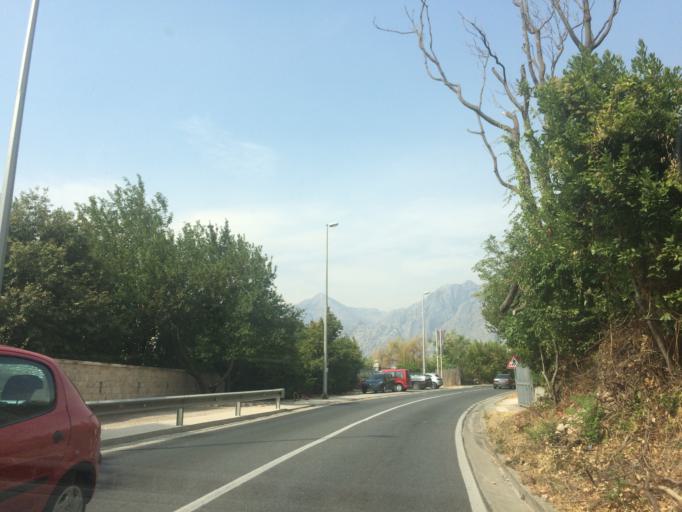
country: ME
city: Dobrota
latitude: 42.4571
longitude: 18.7660
